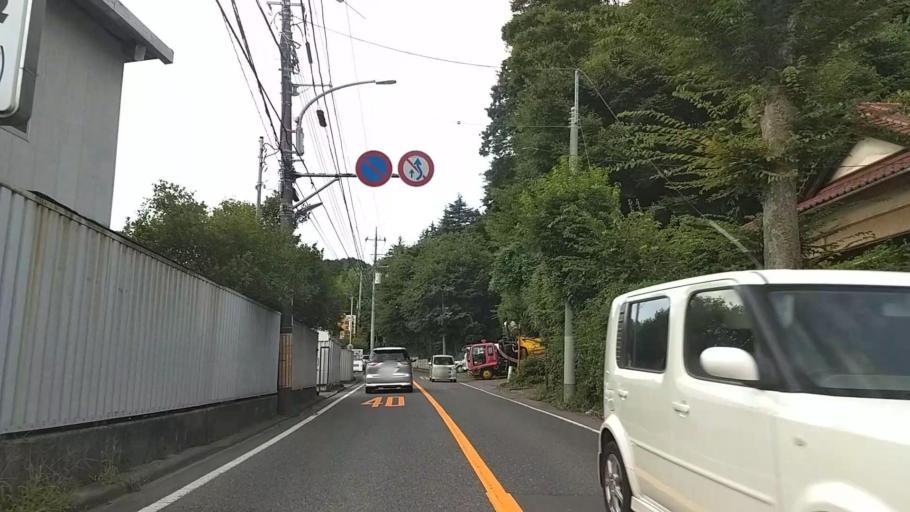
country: JP
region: Kanagawa
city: Yokohama
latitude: 35.4918
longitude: 139.5702
